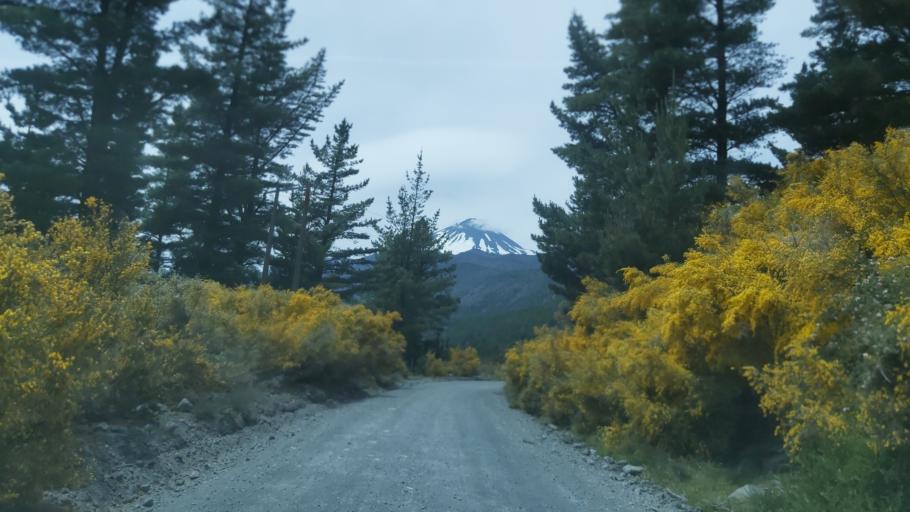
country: AR
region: Neuquen
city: Andacollo
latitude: -37.3972
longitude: -71.4469
